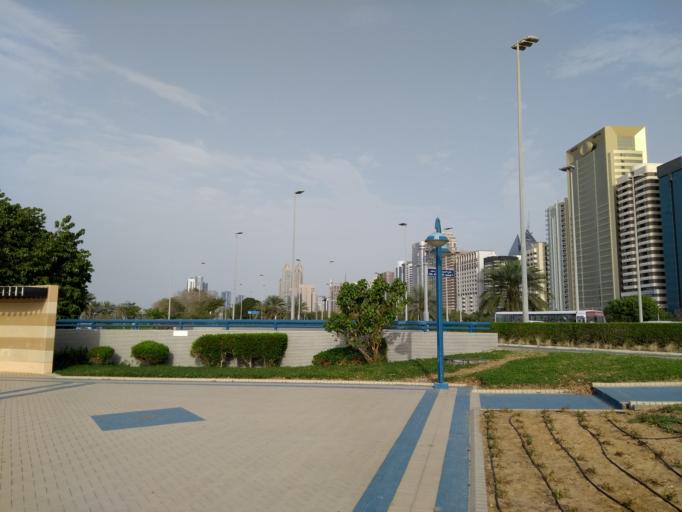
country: AE
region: Abu Dhabi
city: Abu Dhabi
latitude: 24.4908
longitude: 54.3518
